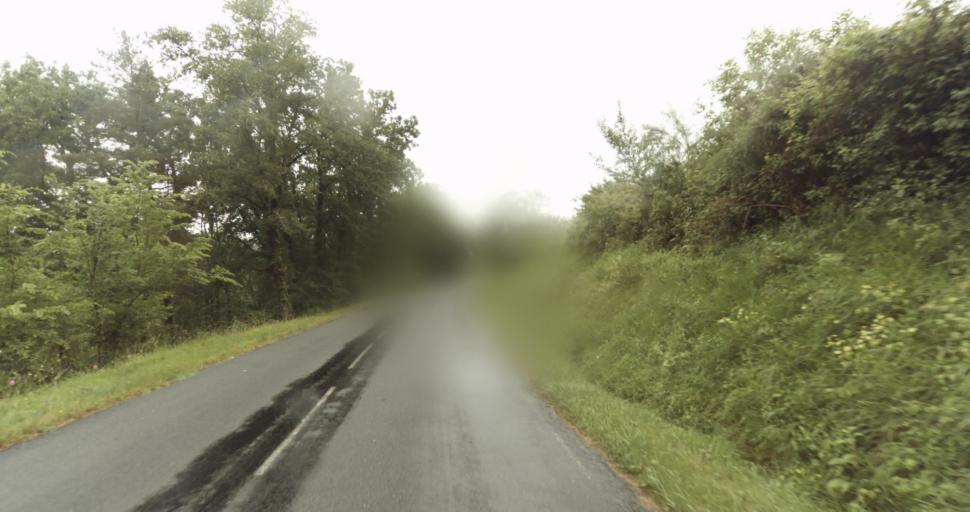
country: FR
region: Aquitaine
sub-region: Departement de la Dordogne
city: Le Bugue
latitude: 44.8217
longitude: 0.8850
